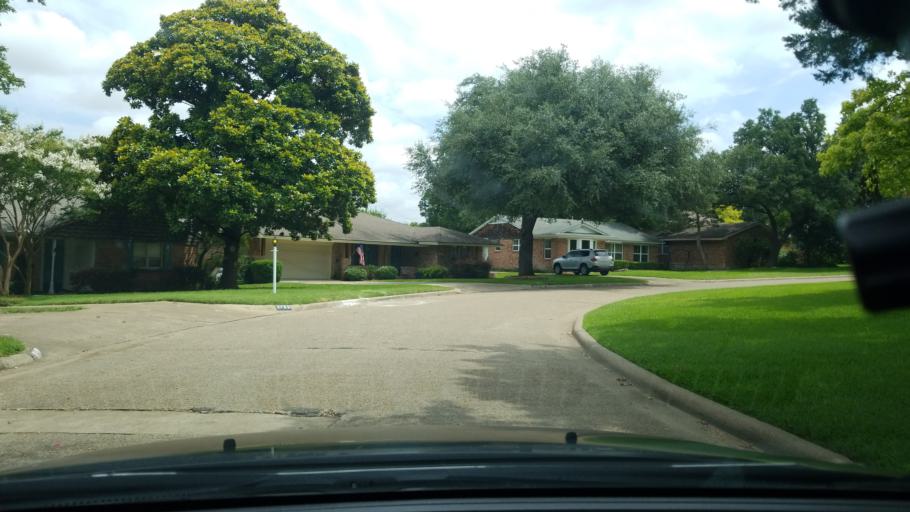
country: US
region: Texas
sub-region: Dallas County
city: Garland
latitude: 32.8249
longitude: -96.6856
